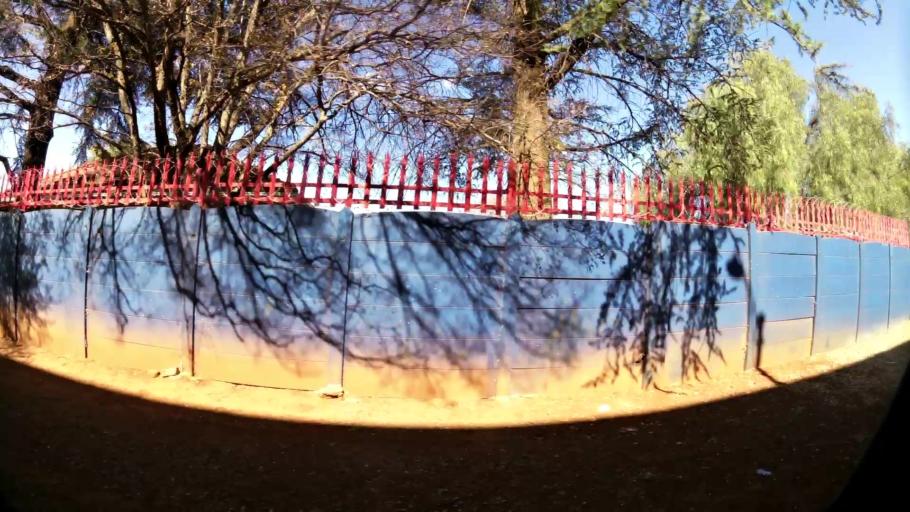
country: ZA
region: Gauteng
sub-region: West Rand District Municipality
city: Carletonville
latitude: -26.3637
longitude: 27.3949
